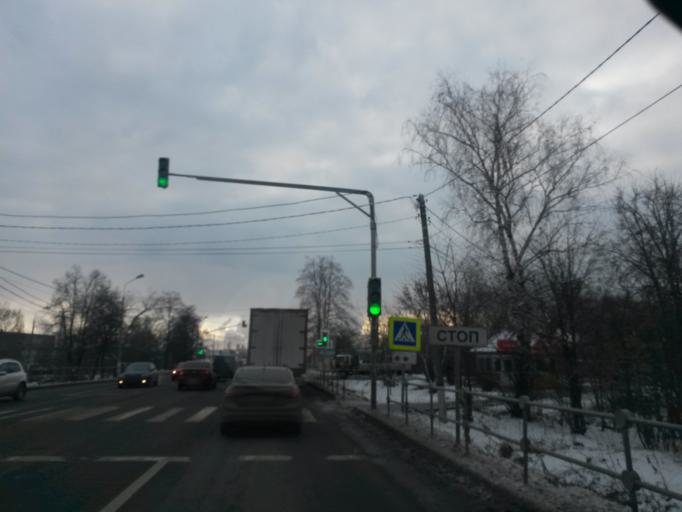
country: RU
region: Moskovskaya
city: Klimovsk
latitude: 55.3581
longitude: 37.5312
